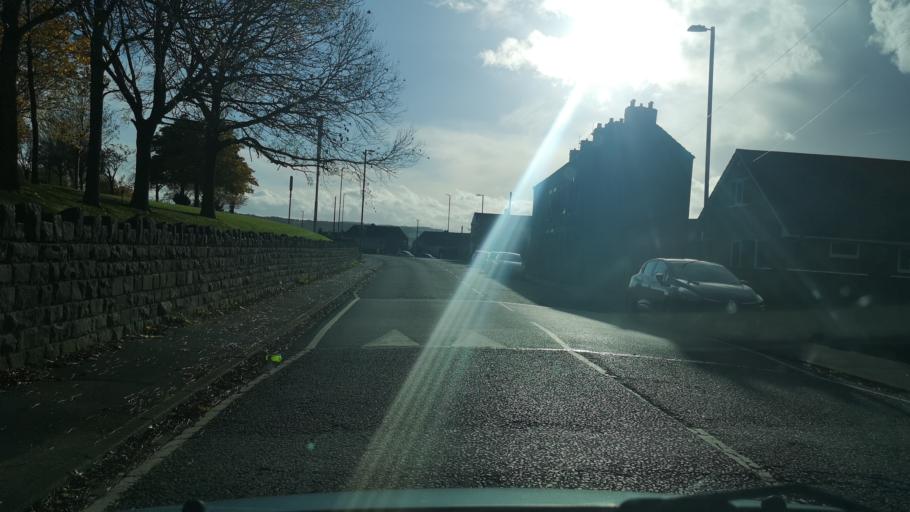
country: GB
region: England
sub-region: Kirklees
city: Batley
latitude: 53.6913
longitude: -1.6536
